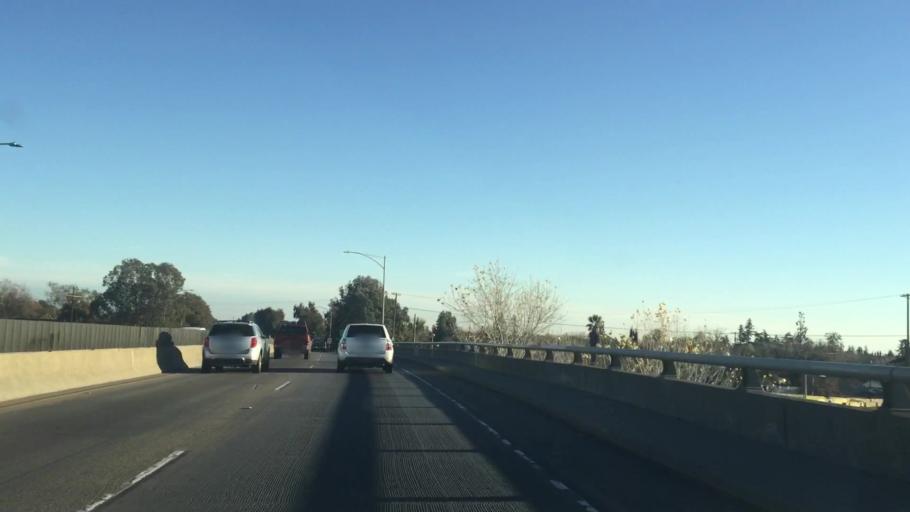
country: US
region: California
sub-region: Yuba County
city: Marysville
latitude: 39.1304
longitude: -121.5867
